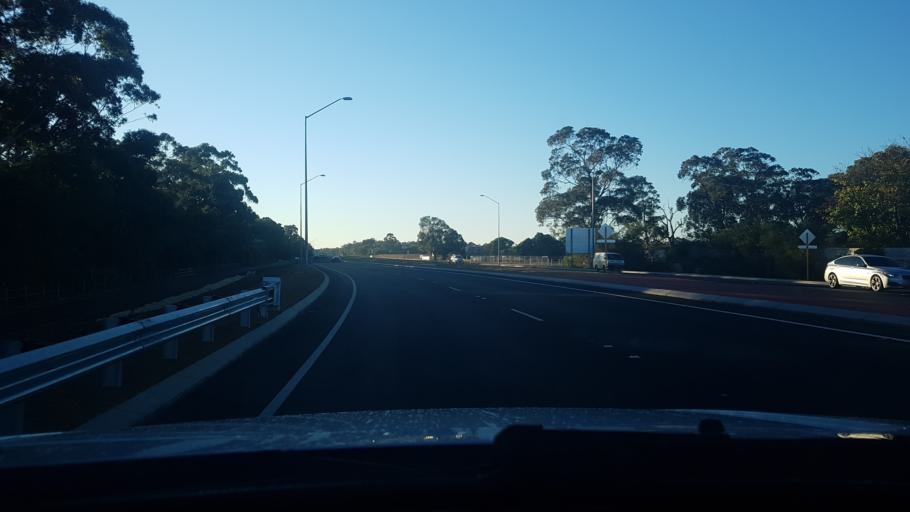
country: AU
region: Western Australia
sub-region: Busselton
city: Busselton
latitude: -33.6708
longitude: 115.3171
